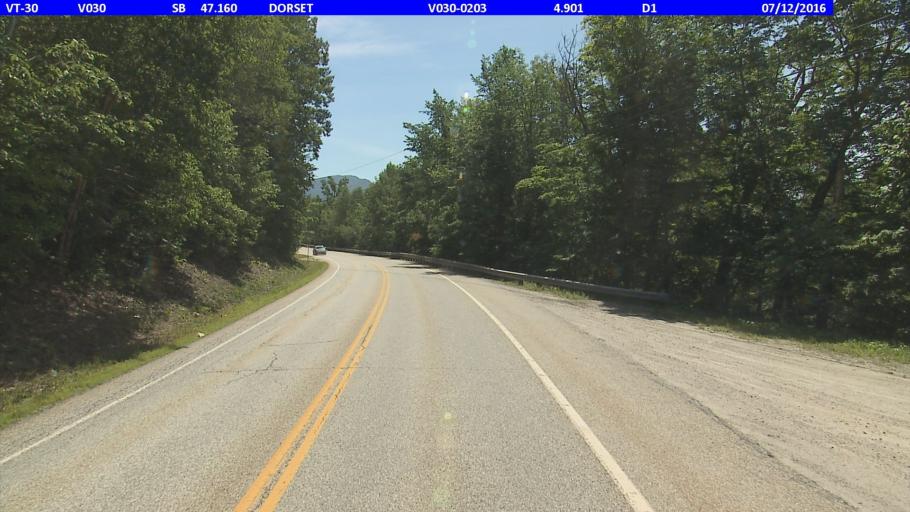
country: US
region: Vermont
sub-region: Bennington County
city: Manchester Center
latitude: 43.2693
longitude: -73.1172
